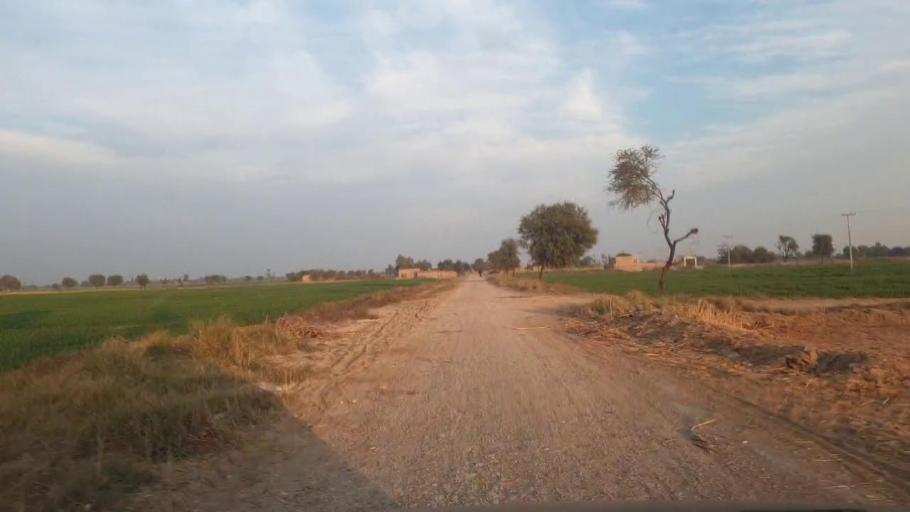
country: PK
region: Sindh
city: Shahpur Chakar
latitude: 26.0528
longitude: 68.5440
